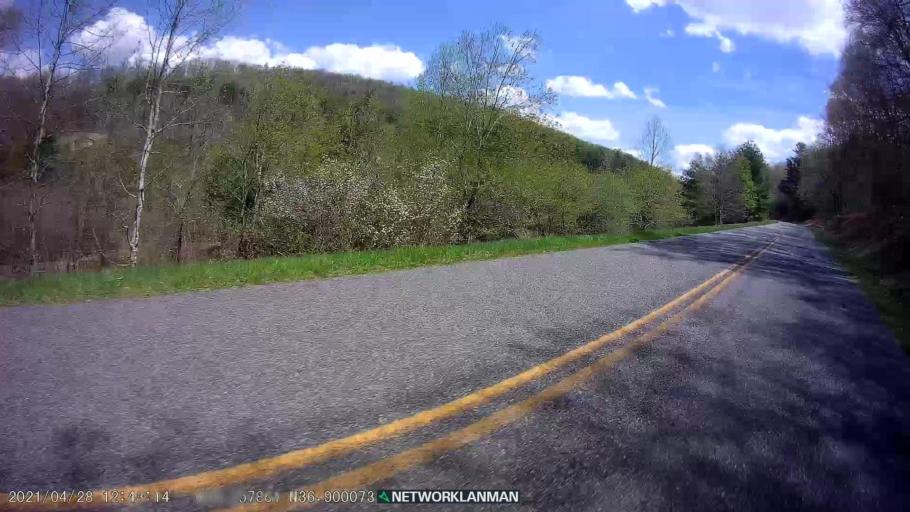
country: US
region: Virginia
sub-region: Floyd County
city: Floyd
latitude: 36.8999
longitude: -80.2579
